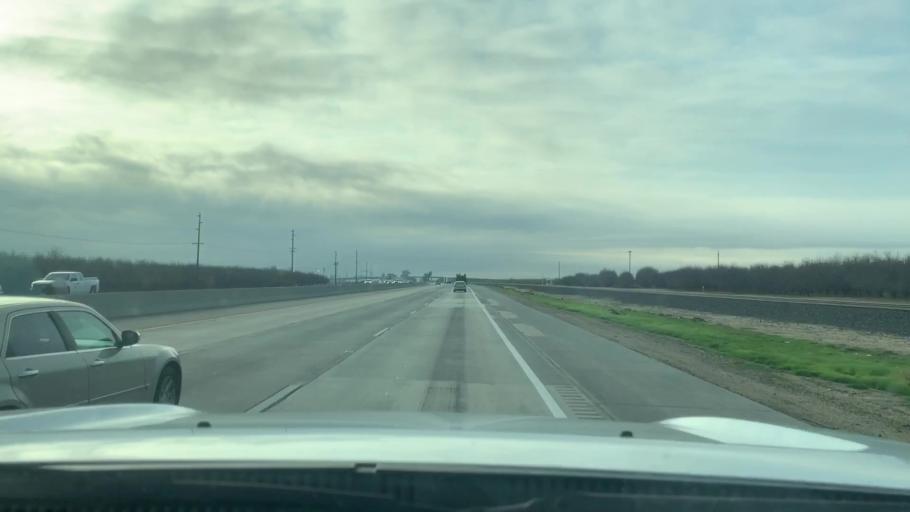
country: US
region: California
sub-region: Kern County
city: Shafter
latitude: 35.5407
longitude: -119.1941
